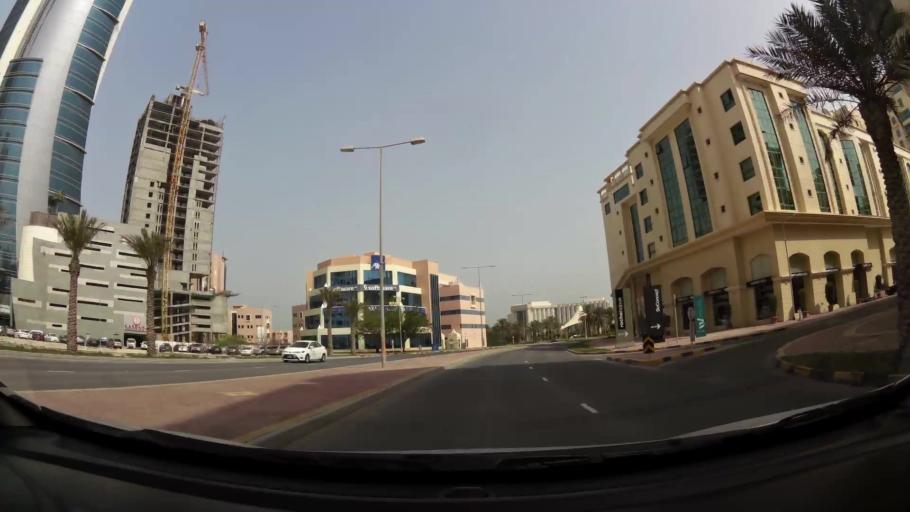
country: BH
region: Manama
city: Jidd Hafs
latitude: 26.2405
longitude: 50.5372
